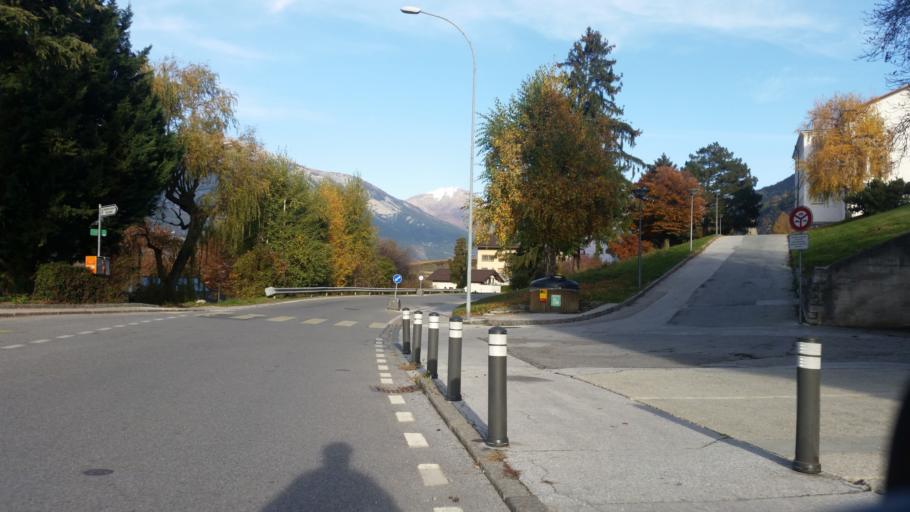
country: CH
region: Valais
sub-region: Sierre District
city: Chalais
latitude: 46.2640
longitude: 7.4998
